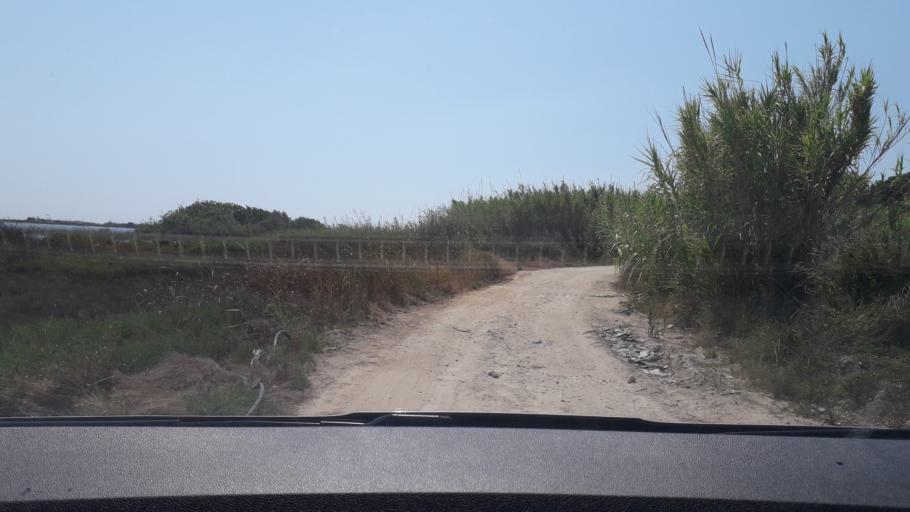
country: GR
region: Ionian Islands
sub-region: Nomos Kerkyras
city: Agios Matthaios
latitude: 39.4553
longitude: 19.8813
